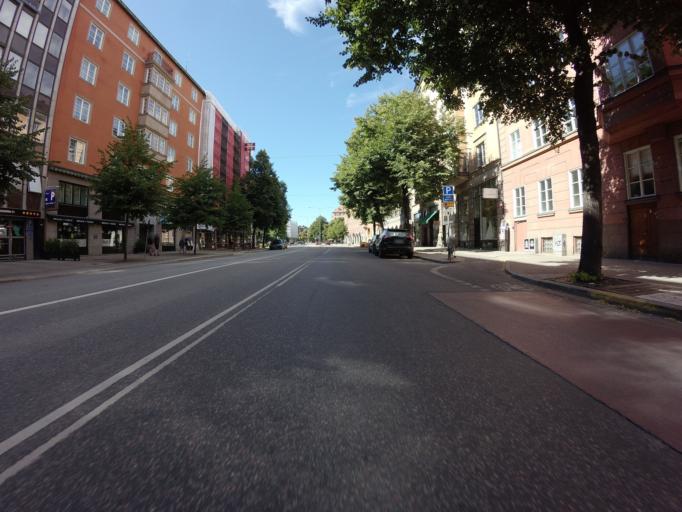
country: SE
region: Stockholm
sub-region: Stockholms Kommun
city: Stockholm
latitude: 59.3397
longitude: 18.0674
